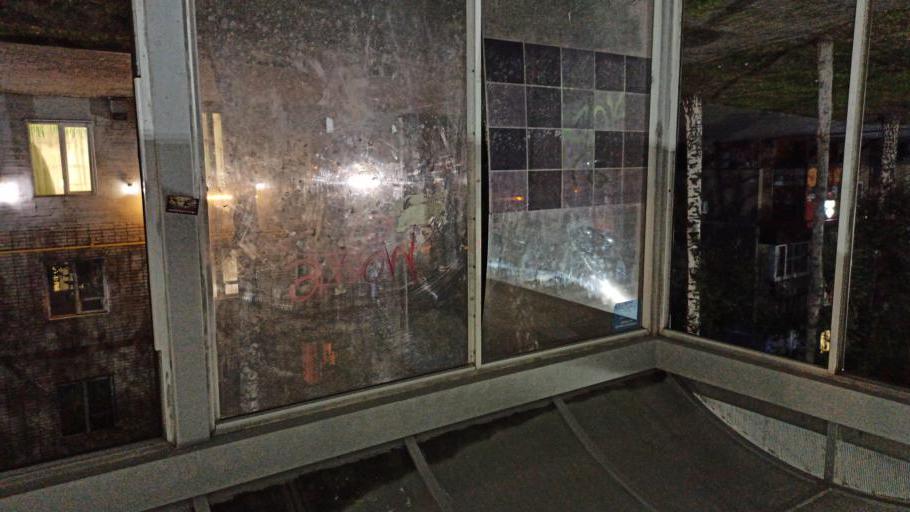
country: RU
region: Tomsk
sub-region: Tomskiy Rayon
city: Tomsk
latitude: 56.4600
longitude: 84.9696
